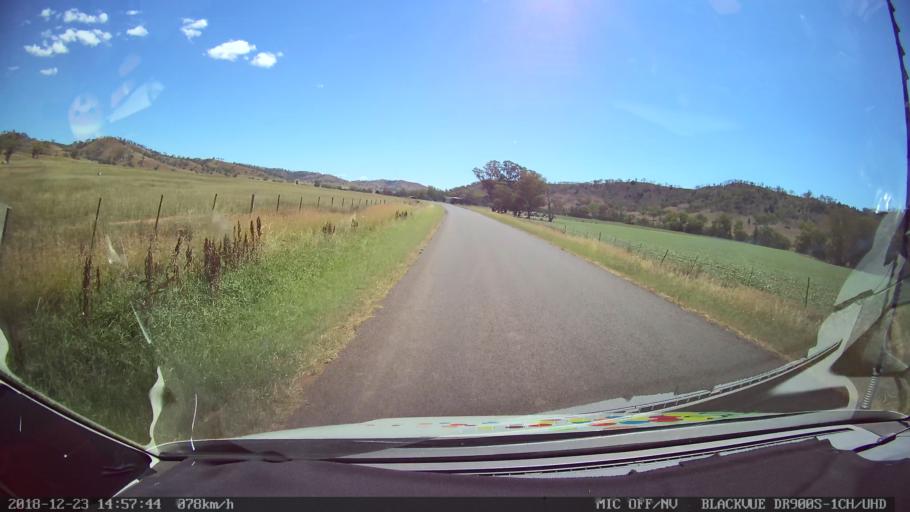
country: AU
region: New South Wales
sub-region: Tamworth Municipality
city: Manilla
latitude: -30.7112
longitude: 150.8209
